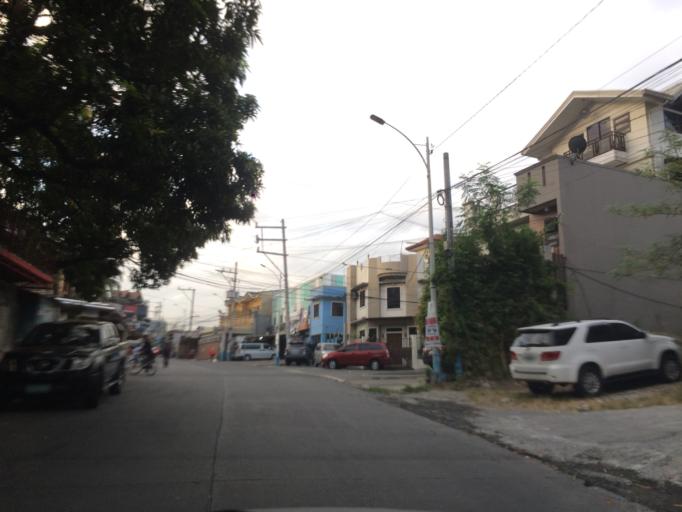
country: PH
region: Calabarzon
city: Bagong Pagasa
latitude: 14.6716
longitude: 121.0251
